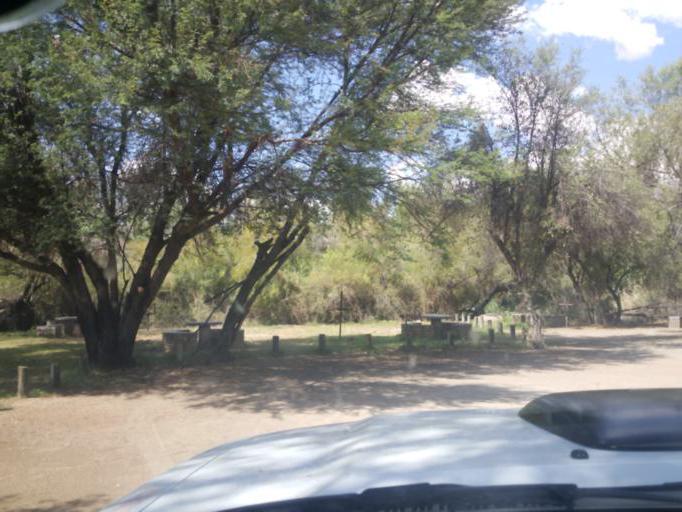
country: ZA
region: Northern Cape
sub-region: Siyanda District Municipality
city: Kakamas
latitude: -28.5954
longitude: 20.3357
